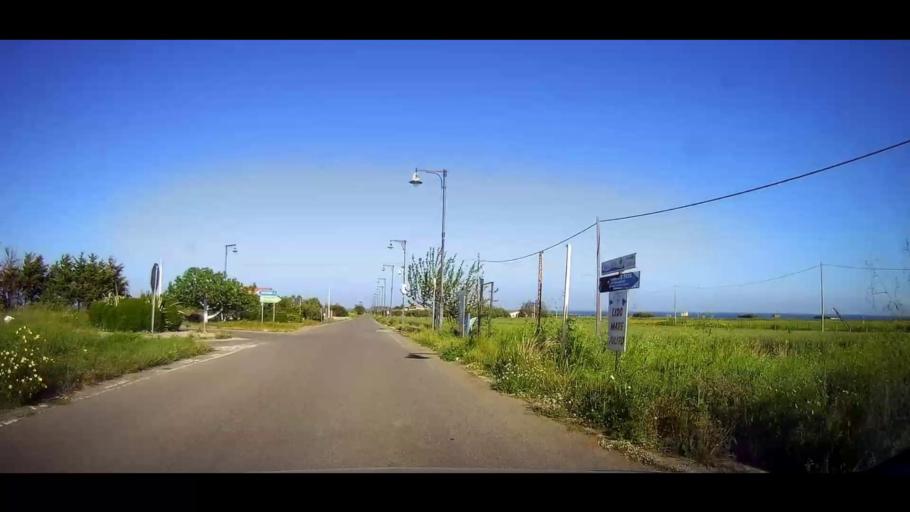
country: IT
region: Calabria
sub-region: Provincia di Crotone
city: Crotone
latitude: 39.0248
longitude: 17.1739
